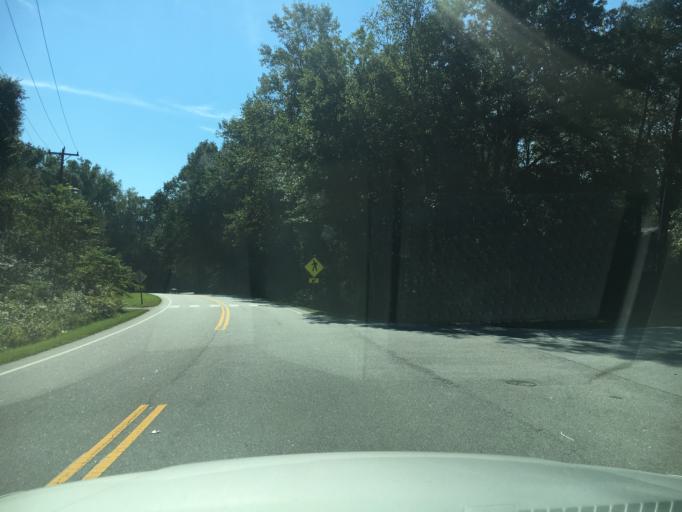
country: US
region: South Carolina
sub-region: Greenville County
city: Taylors
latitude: 34.8855
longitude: -82.2846
